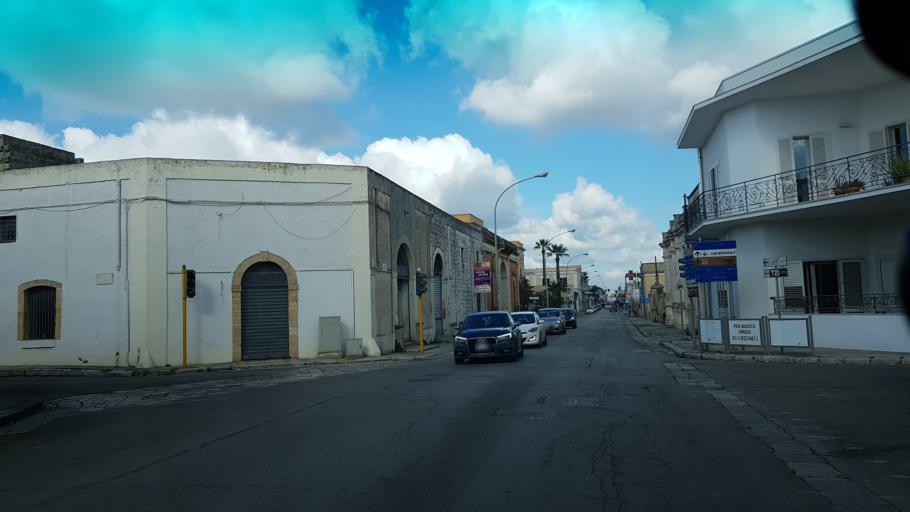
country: IT
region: Apulia
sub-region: Provincia di Lecce
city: Squinzano
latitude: 40.4330
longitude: 18.0424
